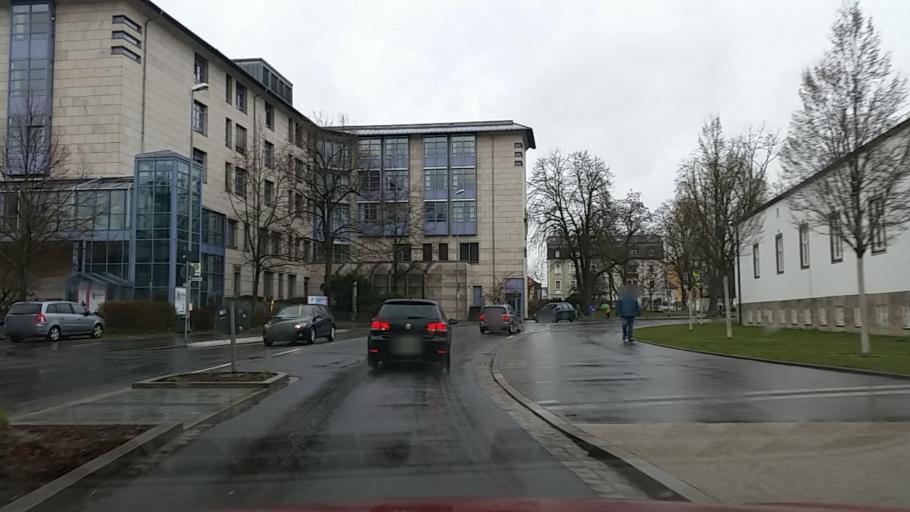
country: DE
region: Bavaria
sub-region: Regierungsbezirk Unterfranken
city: Schweinfurt
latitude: 50.0434
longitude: 10.2266
